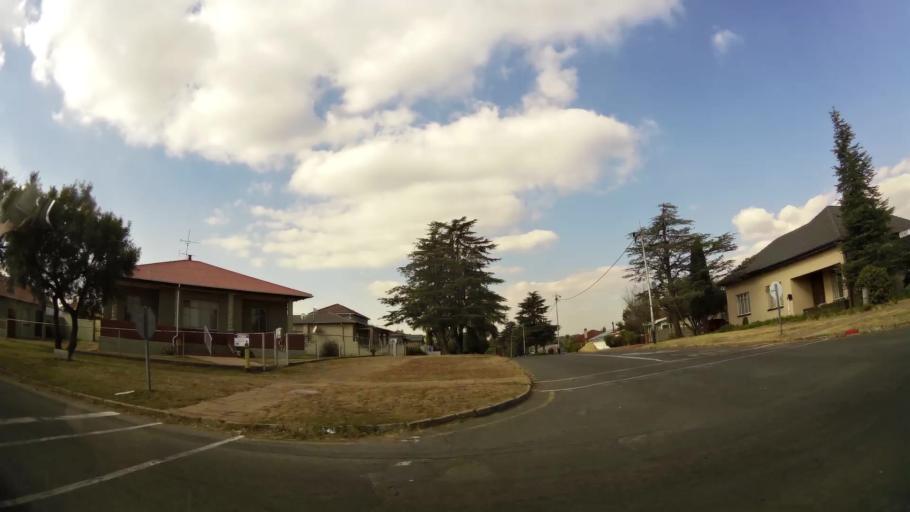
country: ZA
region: Gauteng
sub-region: West Rand District Municipality
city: Krugersdorp
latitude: -26.0909
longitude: 27.7711
